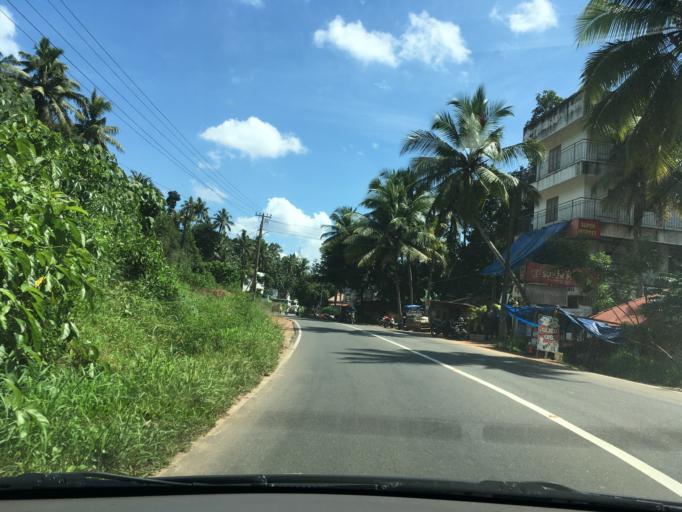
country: IN
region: Kerala
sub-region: Thiruvananthapuram
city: Nedumangad
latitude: 8.5664
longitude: 76.9846
